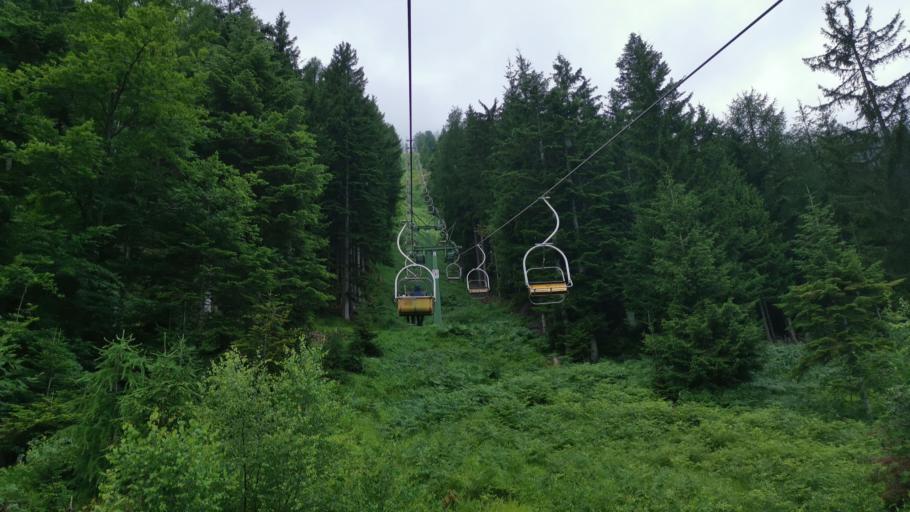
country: AT
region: Tyrol
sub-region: Politischer Bezirk Lienz
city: Leisach
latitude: 46.8236
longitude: 12.7365
